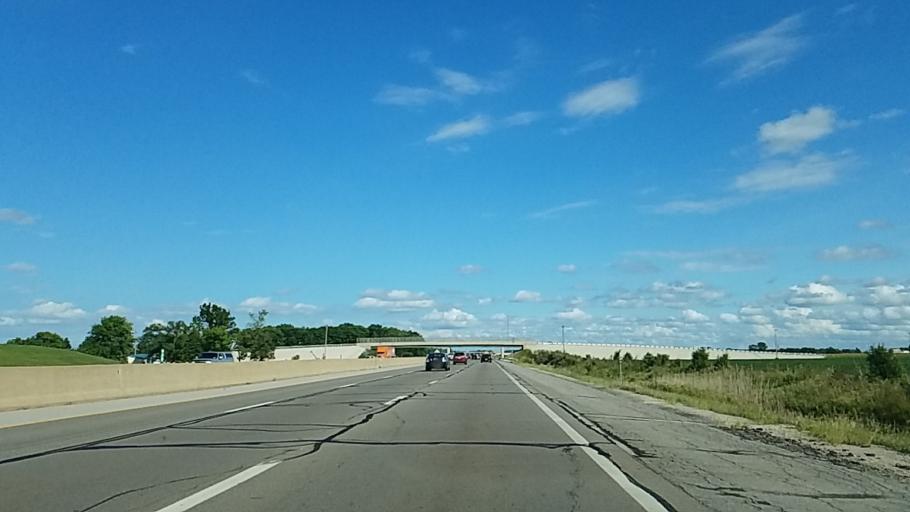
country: US
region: Ohio
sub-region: Sandusky County
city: Fremont
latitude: 41.3919
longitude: -83.0719
